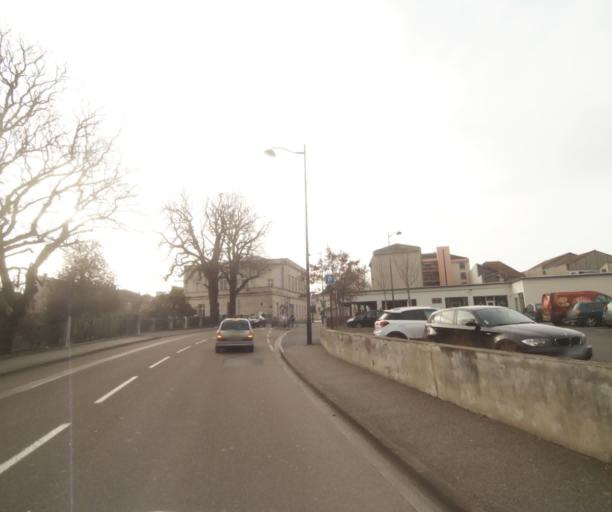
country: FR
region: Champagne-Ardenne
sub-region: Departement de la Haute-Marne
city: Saint-Dizier
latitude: 48.6383
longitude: 4.9473
